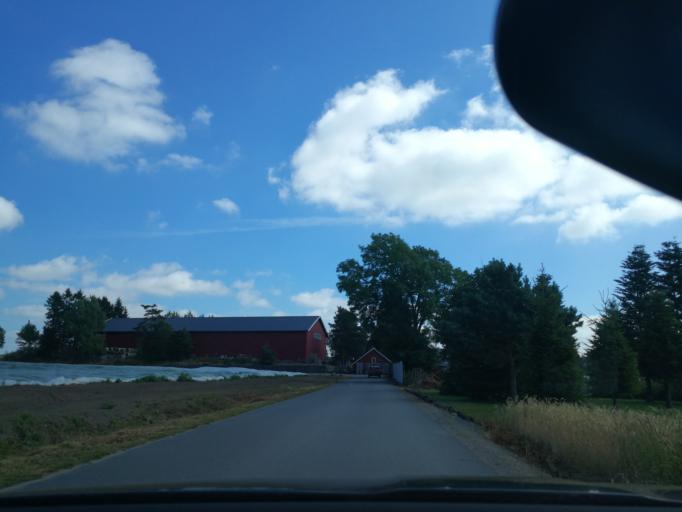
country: NO
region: Vestfold
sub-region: Sandefjord
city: Sandefjord
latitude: 59.1524
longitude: 10.2005
